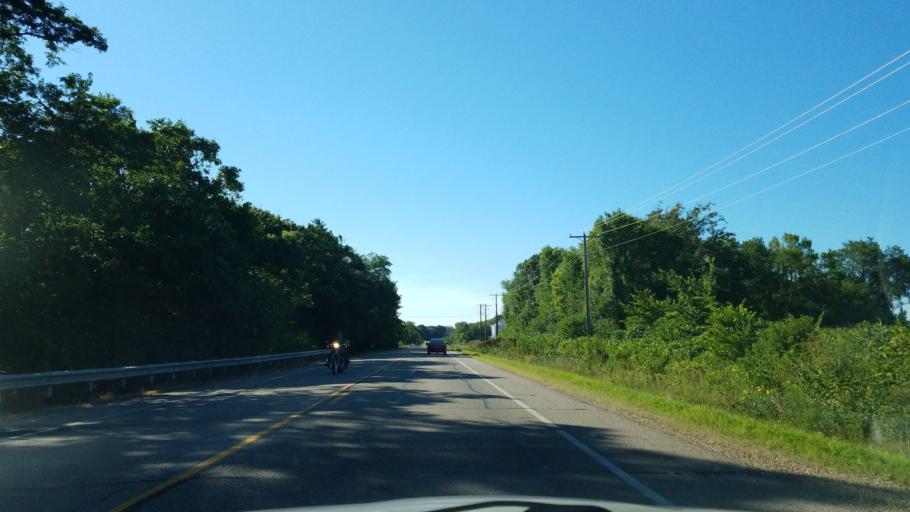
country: US
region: Minnesota
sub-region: Washington County
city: Oak Park Heights
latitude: 45.0450
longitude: -92.7768
